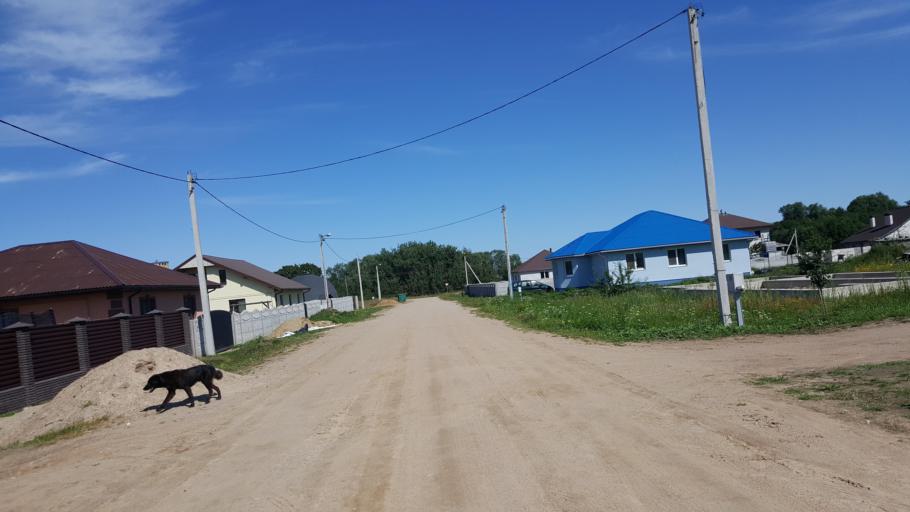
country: BY
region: Brest
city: Charnawchytsy
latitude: 52.2696
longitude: 23.7652
